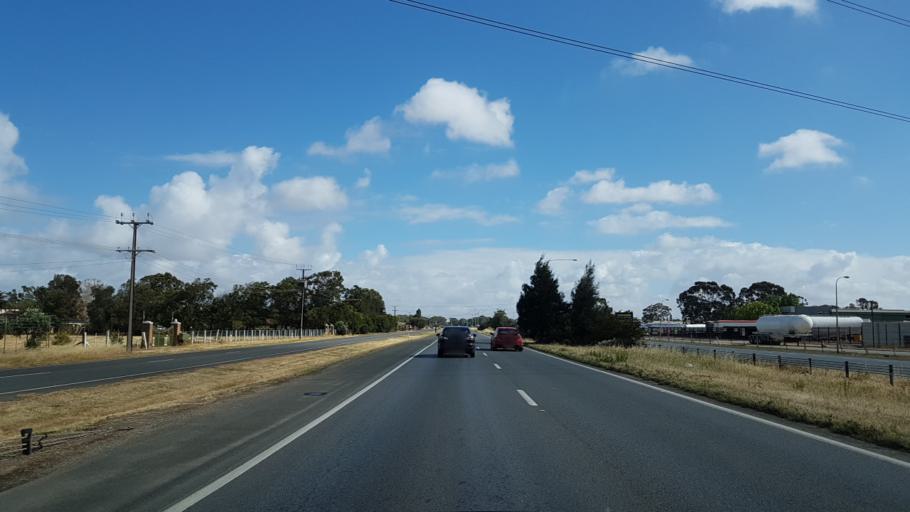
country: AU
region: South Australia
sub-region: Salisbury
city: Salisbury
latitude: -34.7858
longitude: 138.5959
